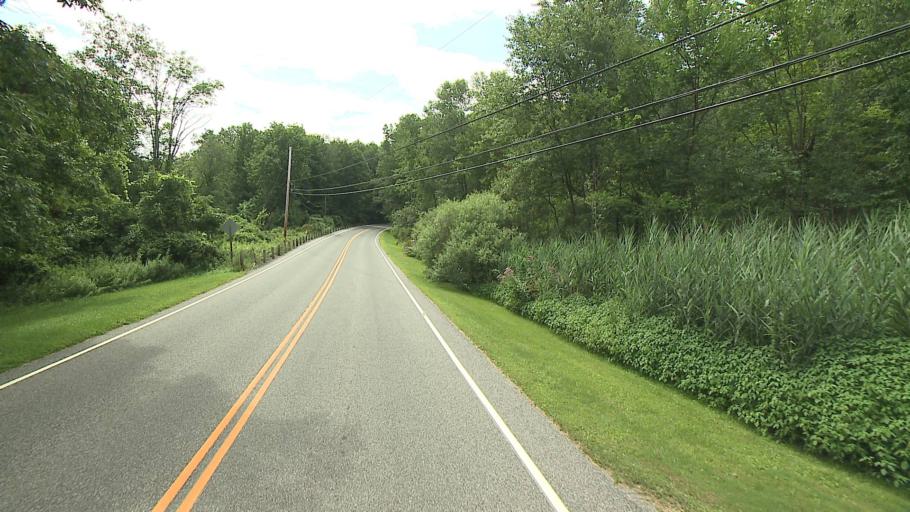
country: US
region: Connecticut
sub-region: Fairfield County
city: Sherman
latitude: 41.6234
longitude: -73.5079
